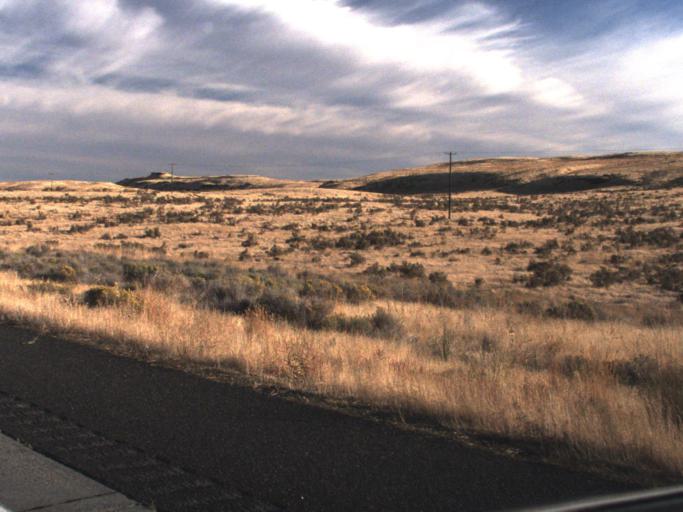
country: US
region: Washington
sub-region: Franklin County
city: Basin City
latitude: 46.4853
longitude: -119.0114
